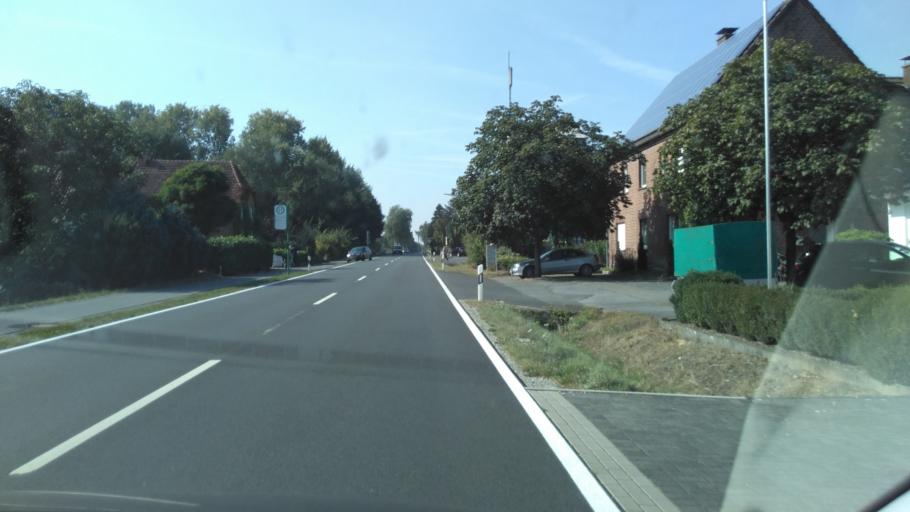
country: DE
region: North Rhine-Westphalia
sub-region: Regierungsbezirk Detmold
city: Verl
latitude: 51.8799
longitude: 8.5532
